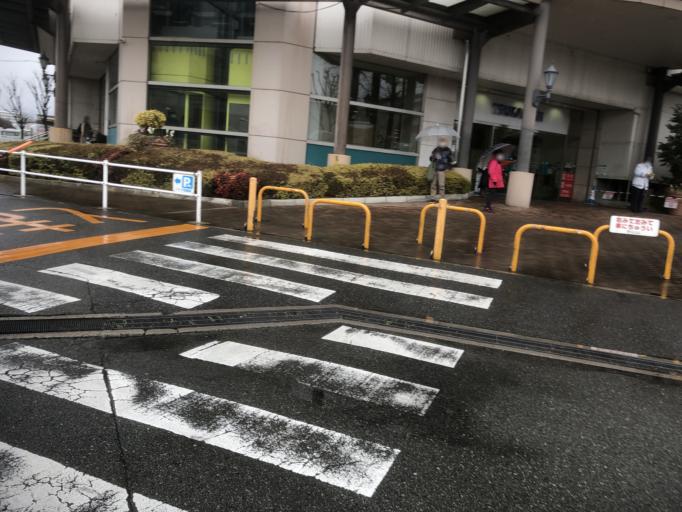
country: JP
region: Hyogo
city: Itami
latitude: 34.7607
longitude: 135.4203
